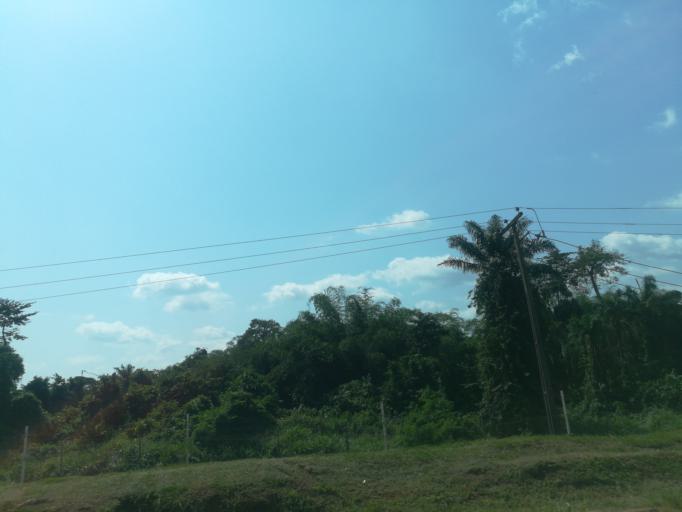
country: NG
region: Oyo
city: Moniya
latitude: 7.5074
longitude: 3.9128
